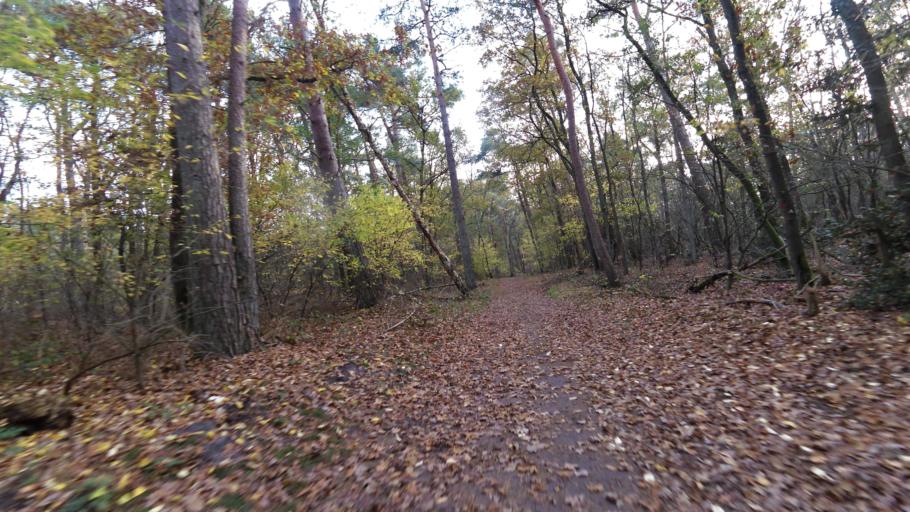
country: NL
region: North Holland
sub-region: Gemeente Hilversum
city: Hilversum
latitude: 52.1958
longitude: 5.1842
